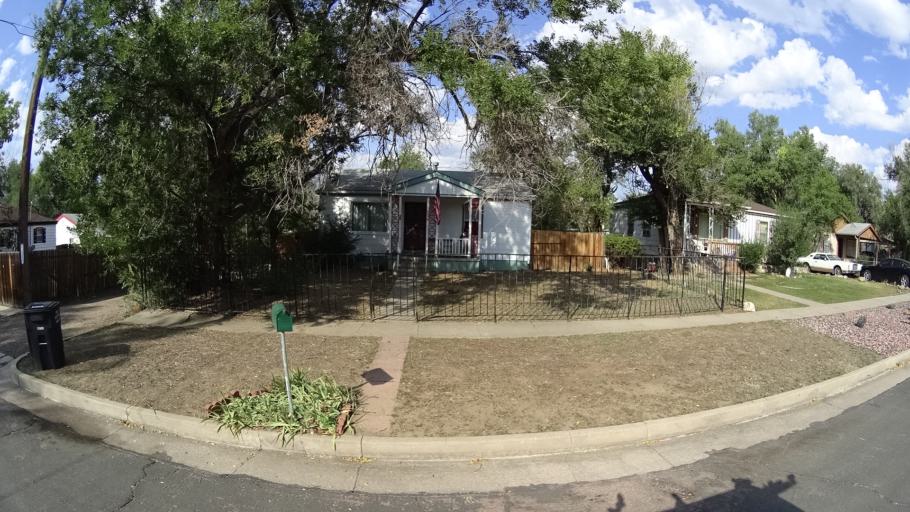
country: US
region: Colorado
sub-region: El Paso County
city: Colorado Springs
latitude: 38.8231
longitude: -104.8028
